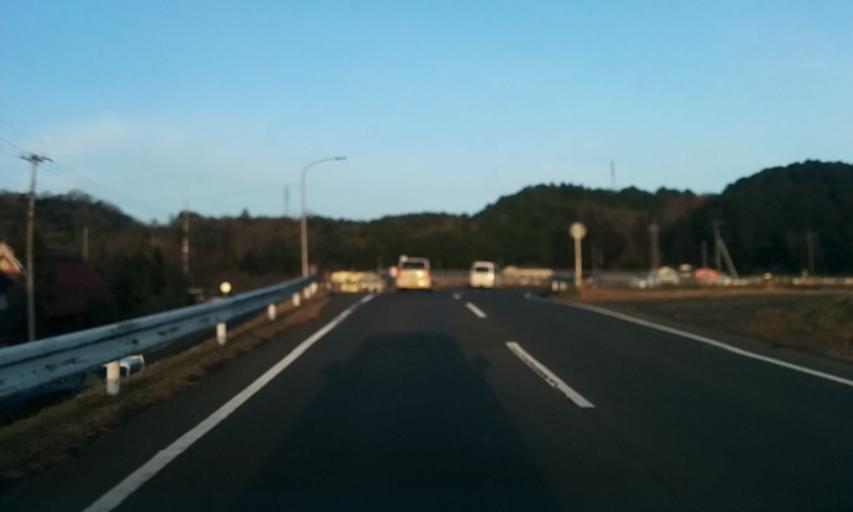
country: JP
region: Kyoto
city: Ayabe
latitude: 35.3135
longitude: 135.2510
